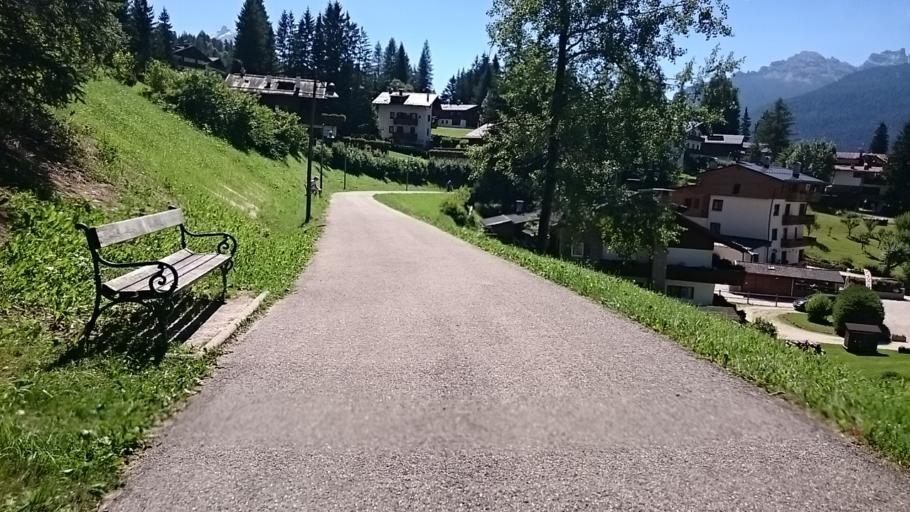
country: IT
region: Veneto
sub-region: Provincia di Belluno
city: Cortina d'Ampezzo
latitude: 46.5282
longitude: 12.1416
